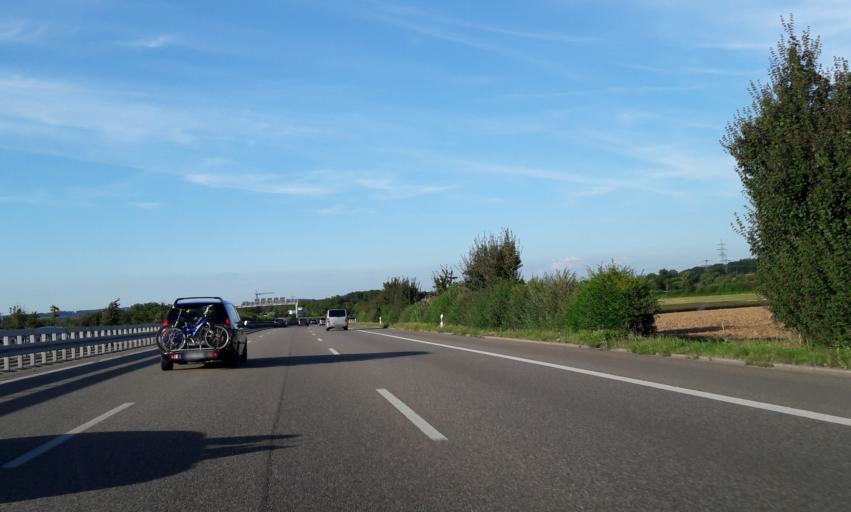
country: DE
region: Baden-Wuerttemberg
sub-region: Regierungsbezirk Stuttgart
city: Freiberg am Neckar
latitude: 48.9448
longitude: 9.1978
